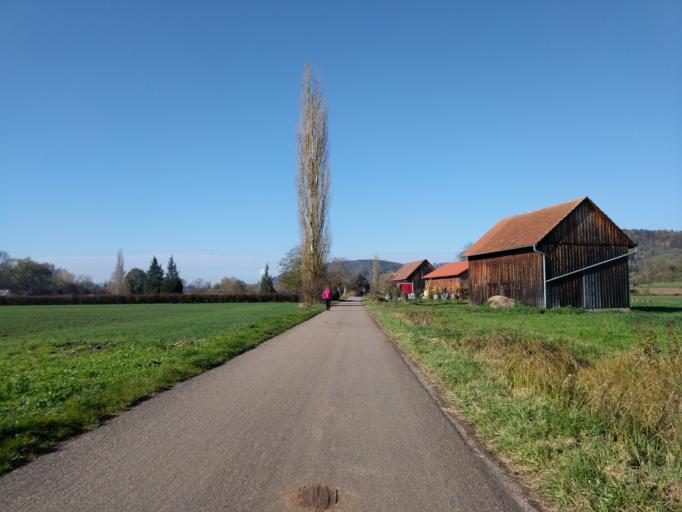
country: DE
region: Baden-Wuerttemberg
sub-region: Tuebingen Region
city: Tuebingen
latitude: 48.5220
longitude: 9.0257
